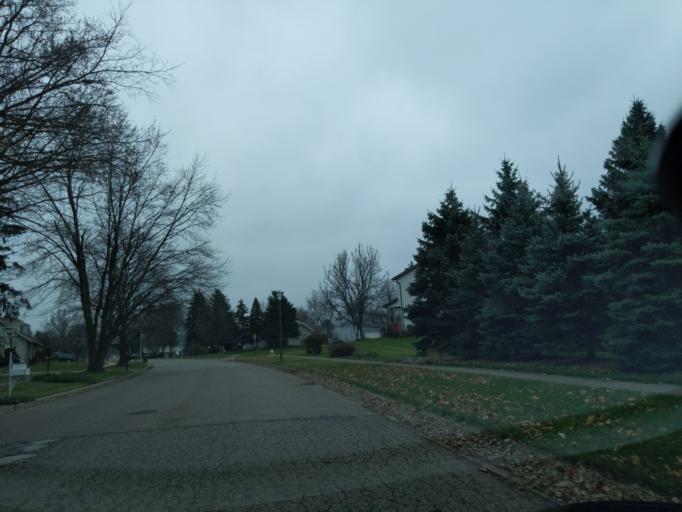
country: US
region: Michigan
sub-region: Eaton County
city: Waverly
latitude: 42.7238
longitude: -84.6296
